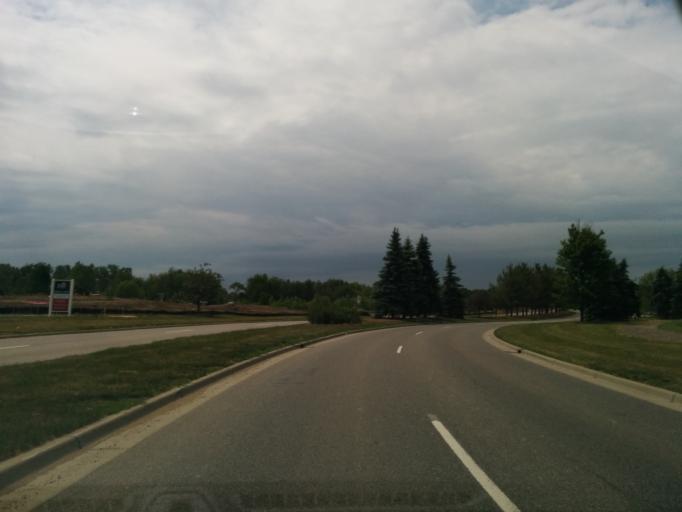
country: US
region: Michigan
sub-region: Oakland County
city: Wolverine Lake
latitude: 42.5654
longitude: -83.4497
